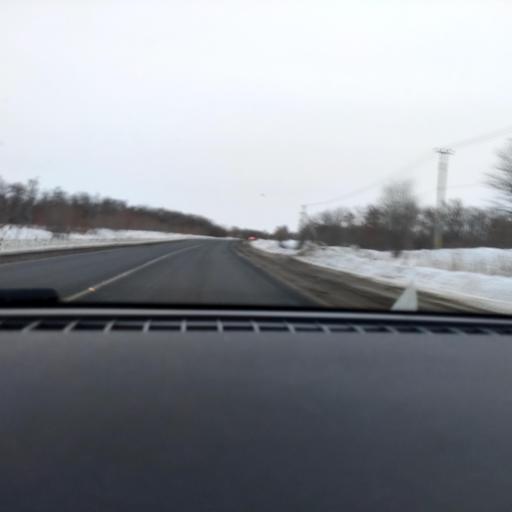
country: RU
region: Samara
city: Dubovyy Umet
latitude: 53.0391
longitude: 50.3333
